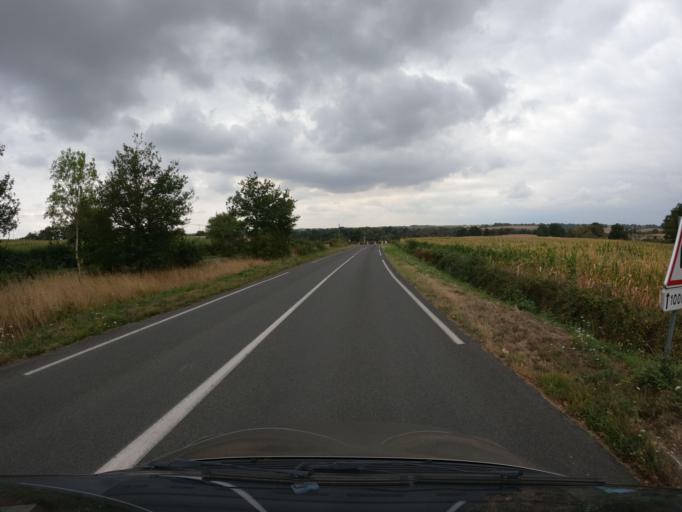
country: FR
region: Pays de la Loire
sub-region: Departement de Maine-et-Loire
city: Le Longeron
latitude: 47.0149
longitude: -1.0721
